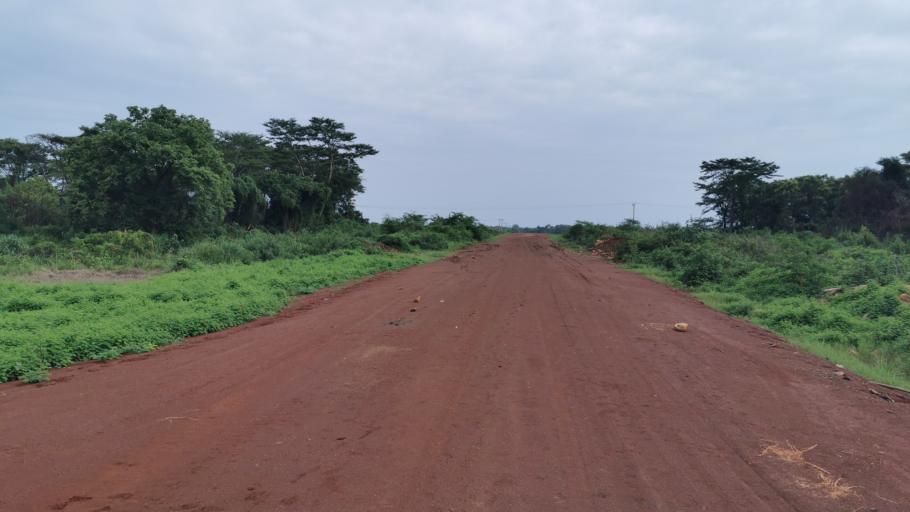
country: ET
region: Gambela
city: Gambela
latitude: 7.8648
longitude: 34.4928
